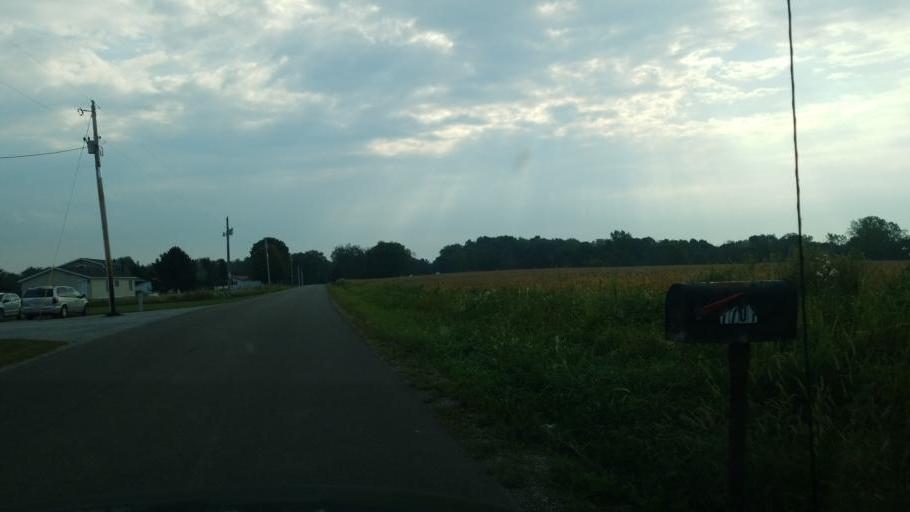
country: US
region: Ohio
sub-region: Knox County
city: Centerburg
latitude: 40.3504
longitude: -82.6512
